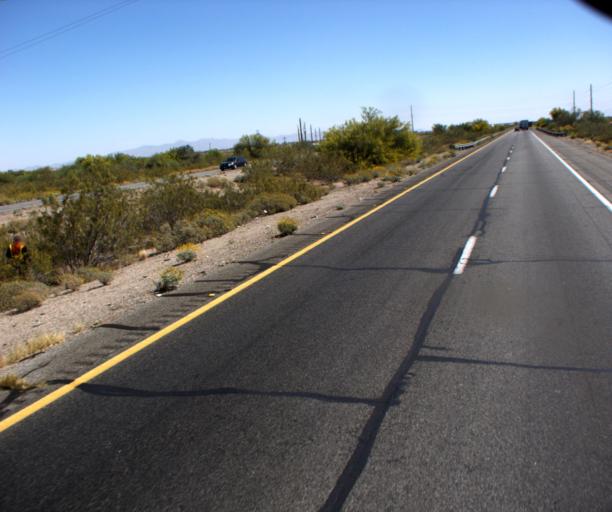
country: US
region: Arizona
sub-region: Maricopa County
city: Buckeye
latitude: 33.4935
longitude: -112.9203
